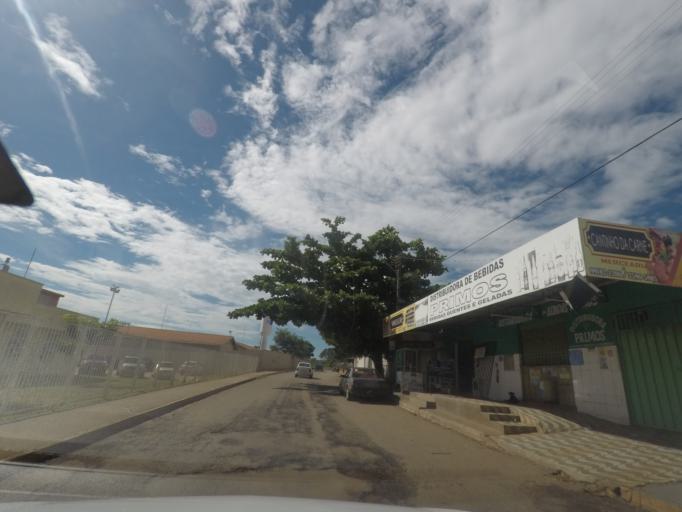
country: BR
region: Goias
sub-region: Aparecida De Goiania
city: Aparecida de Goiania
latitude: -16.7982
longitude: -49.2772
